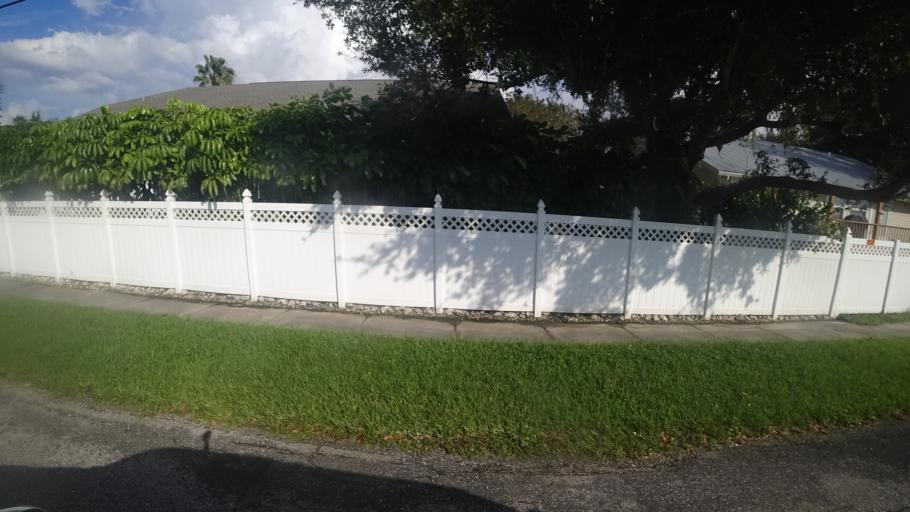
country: US
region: Florida
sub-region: Manatee County
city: West Bradenton
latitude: 27.5283
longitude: -82.6118
